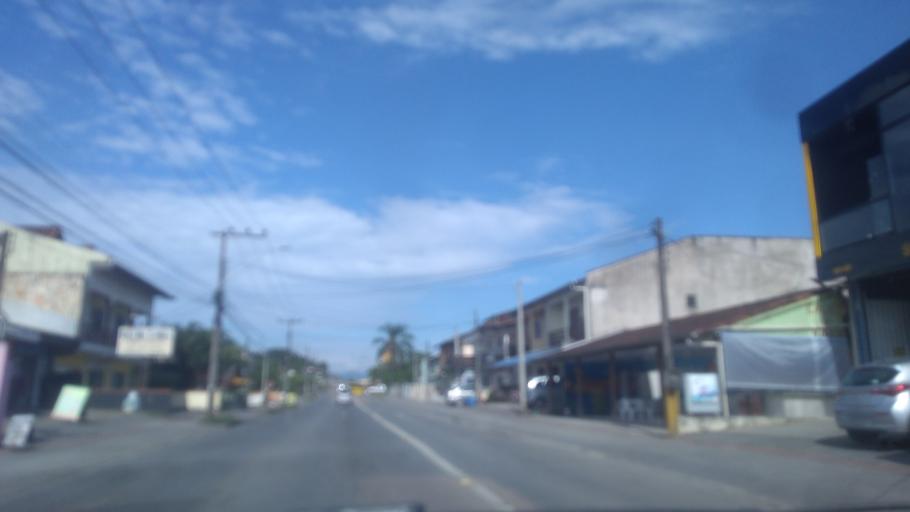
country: BR
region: Santa Catarina
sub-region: Joinville
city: Joinville
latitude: -26.3195
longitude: -48.8202
